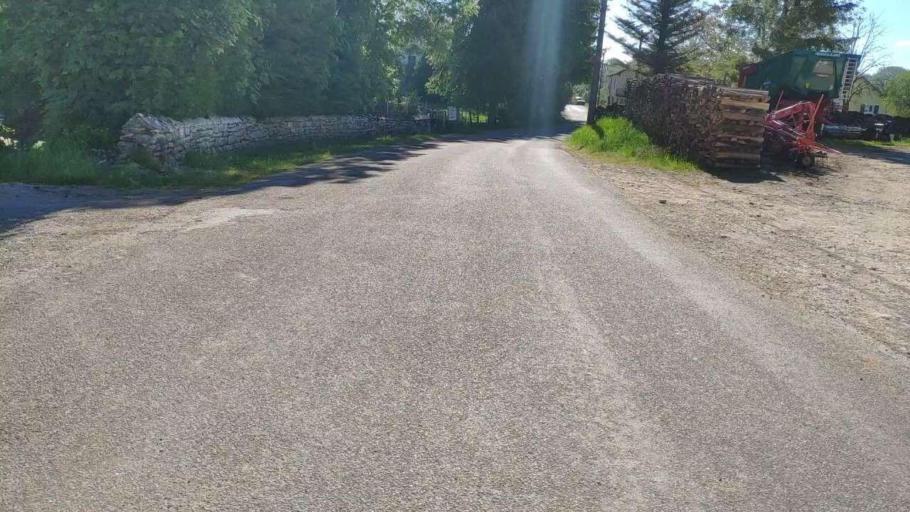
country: FR
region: Franche-Comte
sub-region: Departement du Jura
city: Perrigny
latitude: 46.6857
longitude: 5.6608
